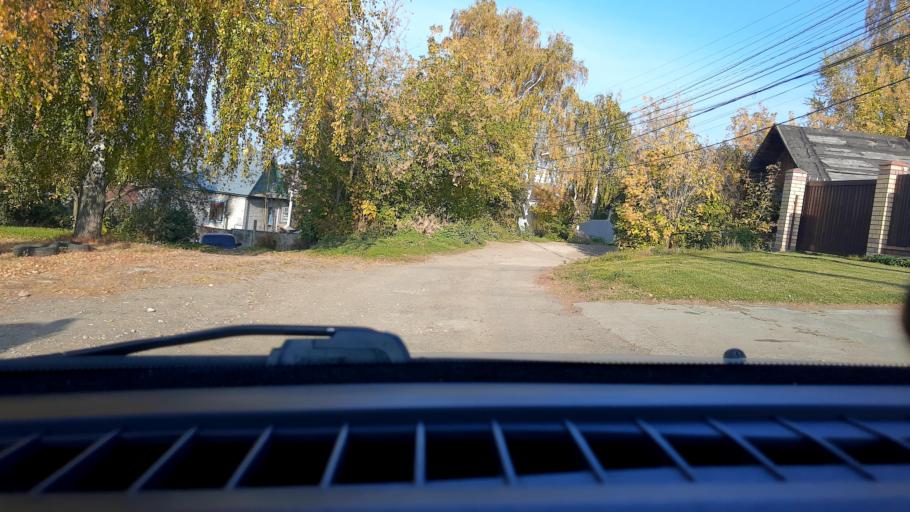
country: RU
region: Nizjnij Novgorod
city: Nizhniy Novgorod
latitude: 56.2519
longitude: 43.9931
